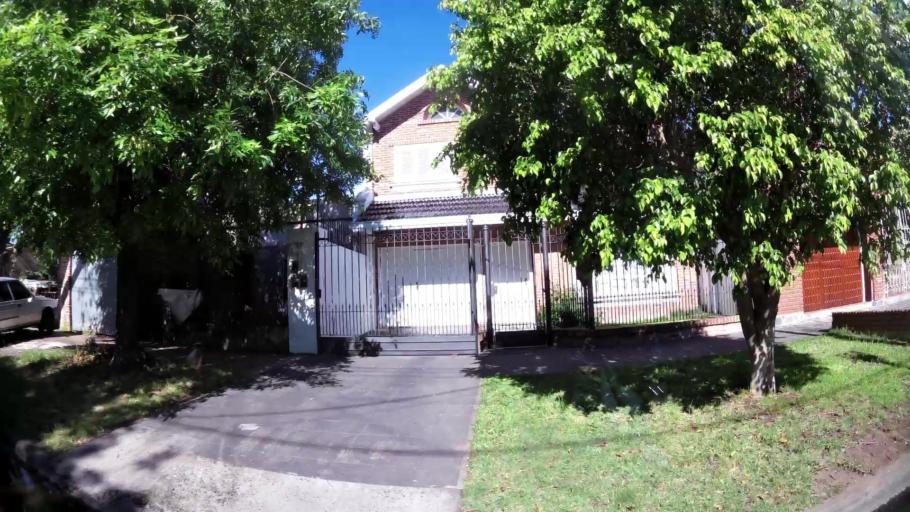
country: AR
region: Buenos Aires
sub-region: Partido de Lomas de Zamora
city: Lomas de Zamora
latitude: -34.7553
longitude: -58.4181
